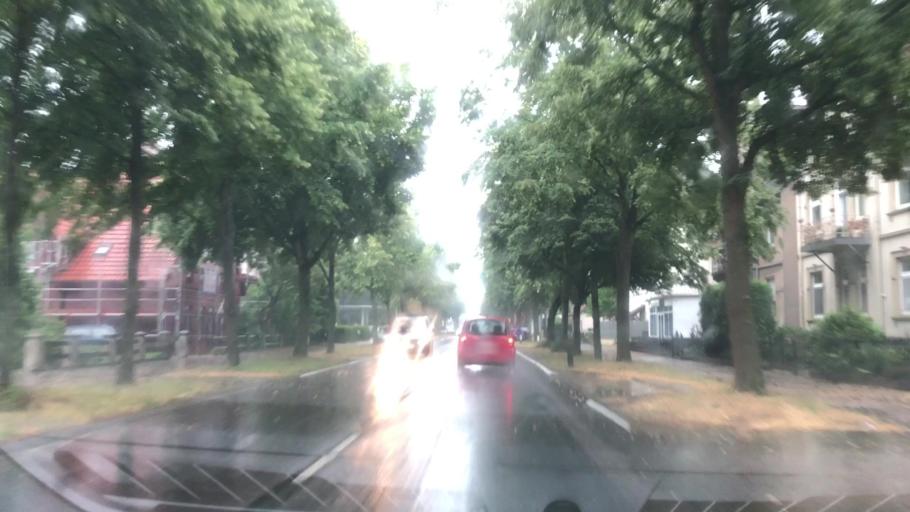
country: DE
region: North Rhine-Westphalia
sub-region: Regierungsbezirk Detmold
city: Minden
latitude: 52.2863
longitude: 8.9458
